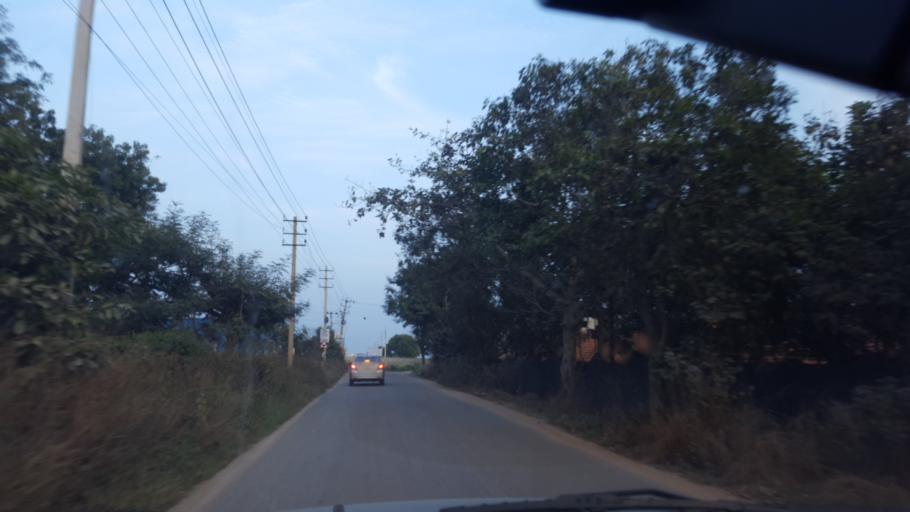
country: IN
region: Karnataka
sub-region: Bangalore Rural
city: Hoskote
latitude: 13.0764
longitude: 77.7033
